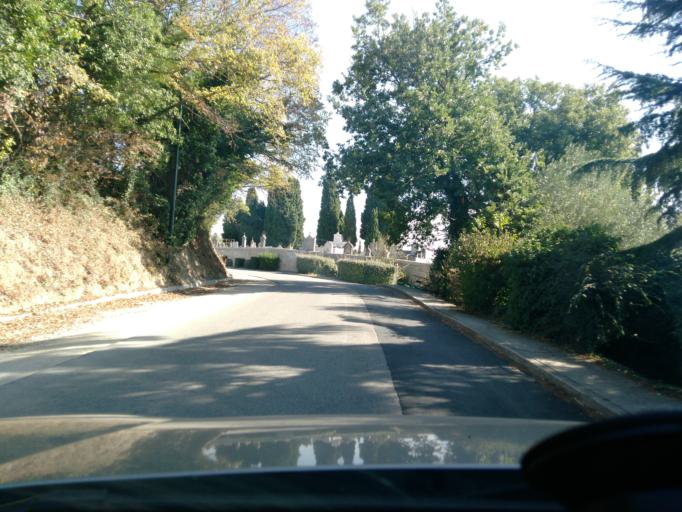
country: FR
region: Rhone-Alpes
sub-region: Departement de la Drome
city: Montboucher-sur-Jabron
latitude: 44.5495
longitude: 4.8014
